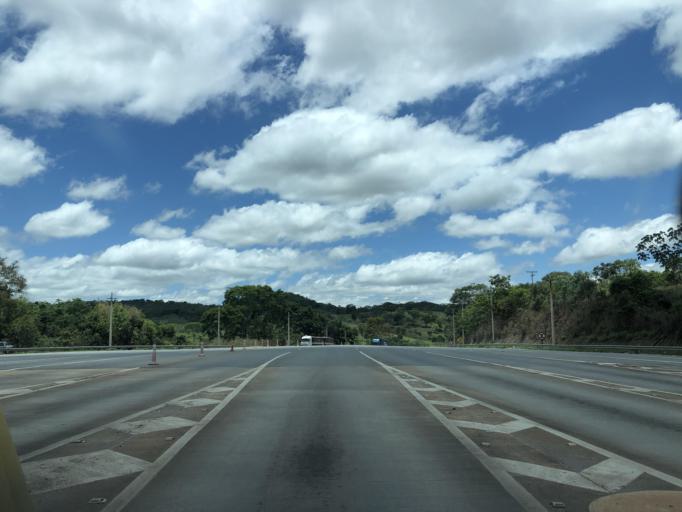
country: BR
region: Goias
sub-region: Abadiania
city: Abadiania
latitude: -16.1158
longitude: -48.5907
